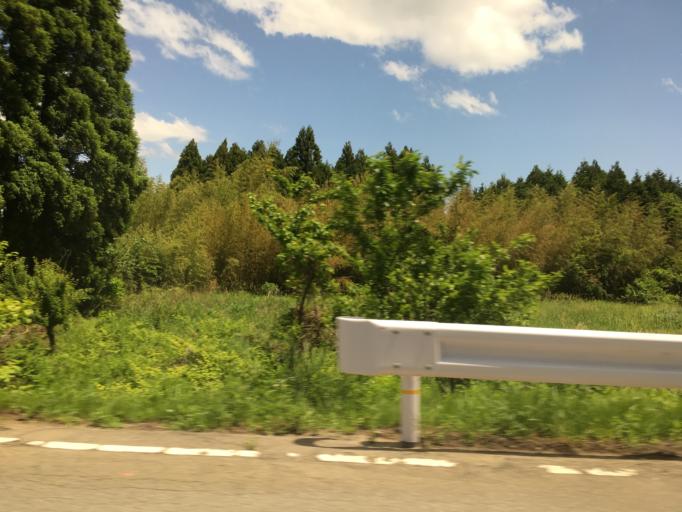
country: JP
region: Fukushima
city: Namie
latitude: 37.4823
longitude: 141.0133
